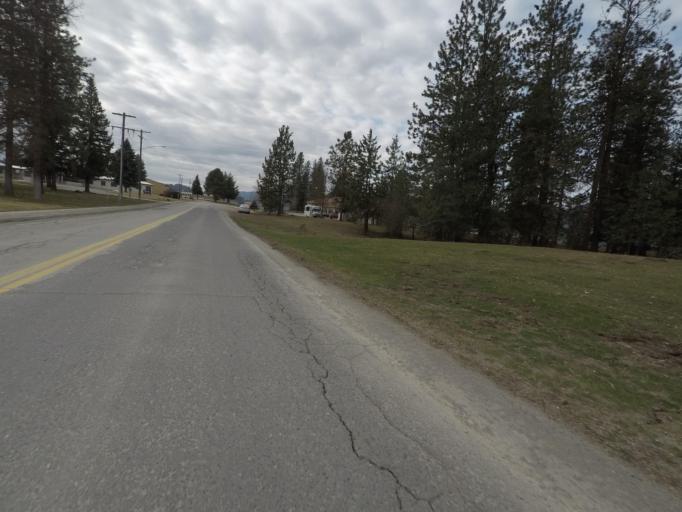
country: US
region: Washington
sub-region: Stevens County
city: Colville
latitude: 48.5443
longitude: -117.8881
